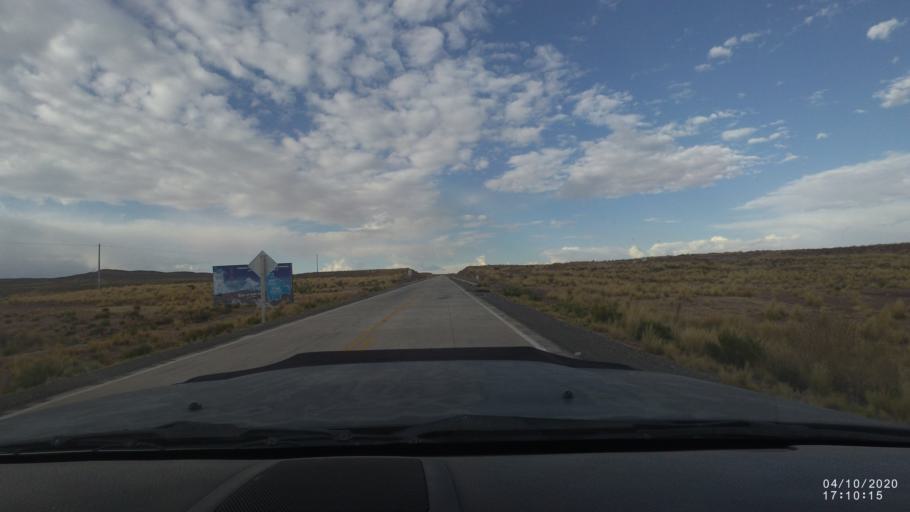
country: BO
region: Oruro
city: Oruro
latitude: -18.3334
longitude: -67.5857
